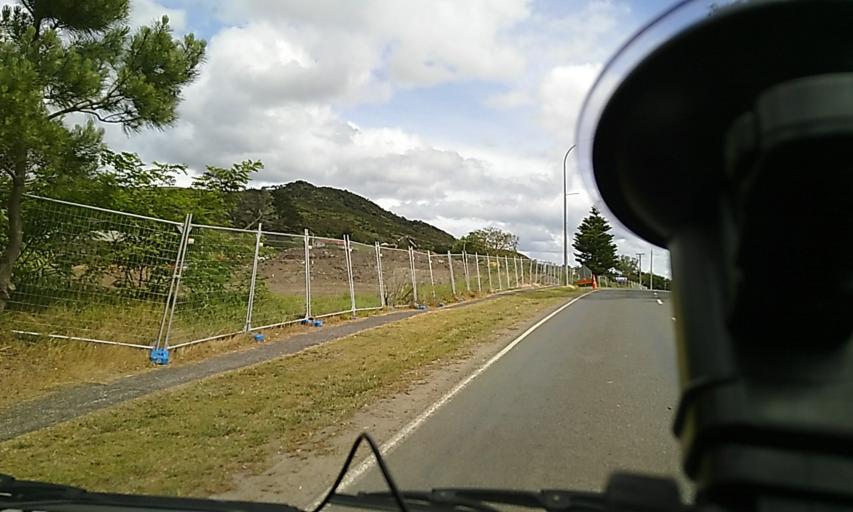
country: NZ
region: Northland
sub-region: Far North District
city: Ahipara
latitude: -35.5064
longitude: 173.3903
